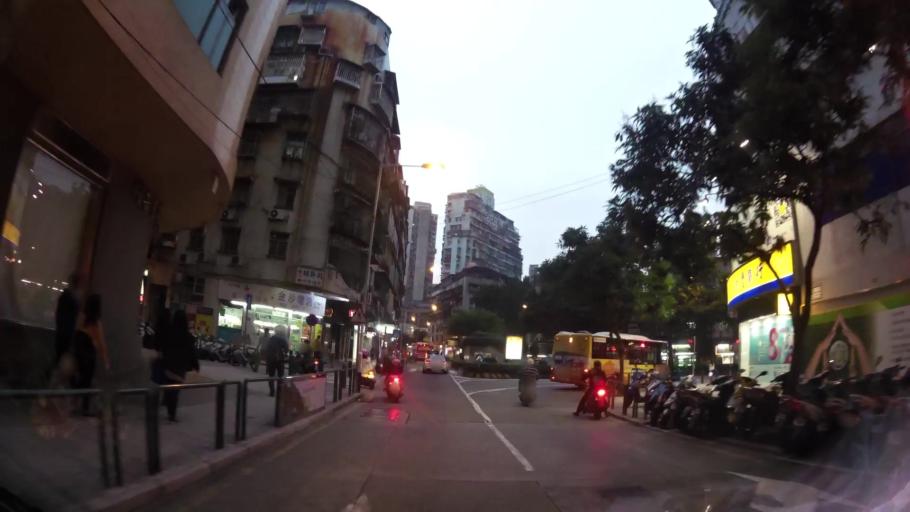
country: MO
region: Macau
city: Macau
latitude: 22.2084
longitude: 113.5497
